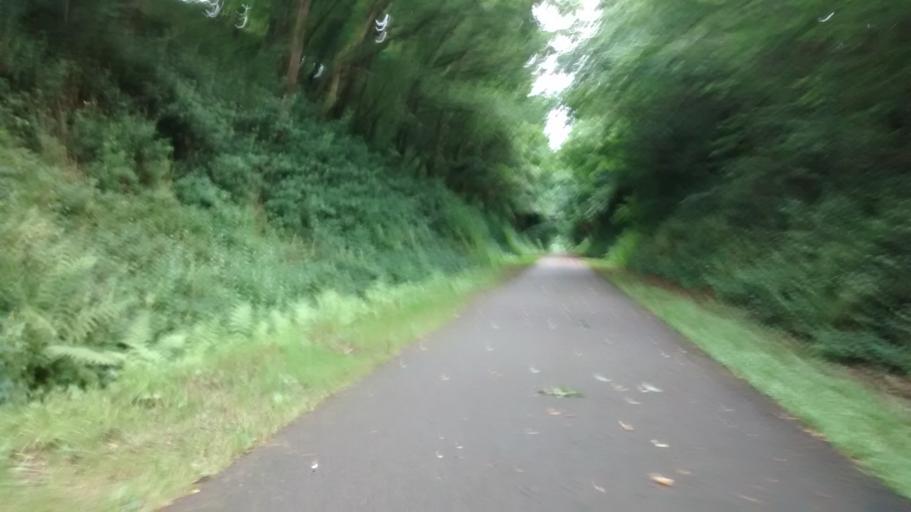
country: FR
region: Brittany
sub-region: Departement du Morbihan
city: Malestroit
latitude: 47.8047
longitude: -2.4006
